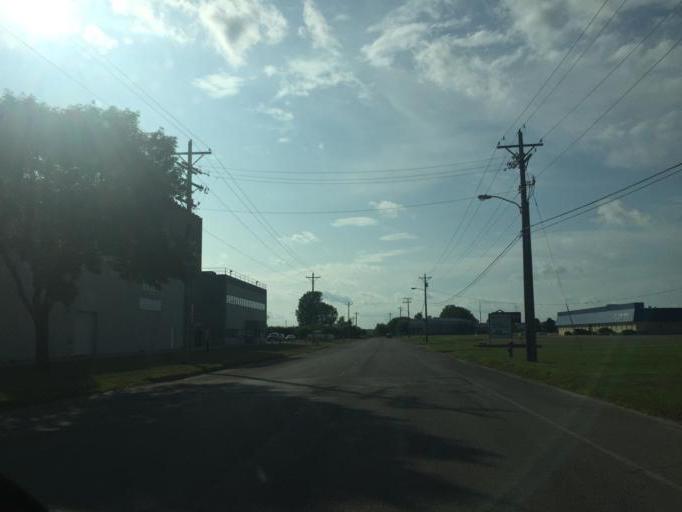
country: US
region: Minnesota
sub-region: Olmsted County
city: Rochester
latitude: 44.0352
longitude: -92.4966
